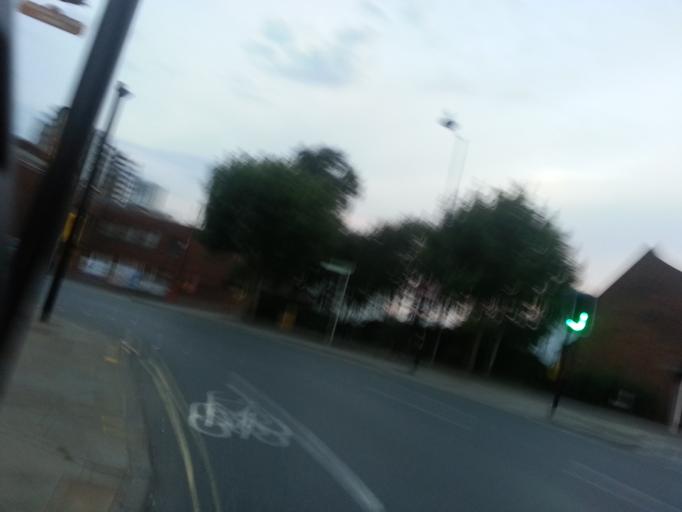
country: GB
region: England
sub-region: Suffolk
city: Ipswich
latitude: 52.0534
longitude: 1.1609
